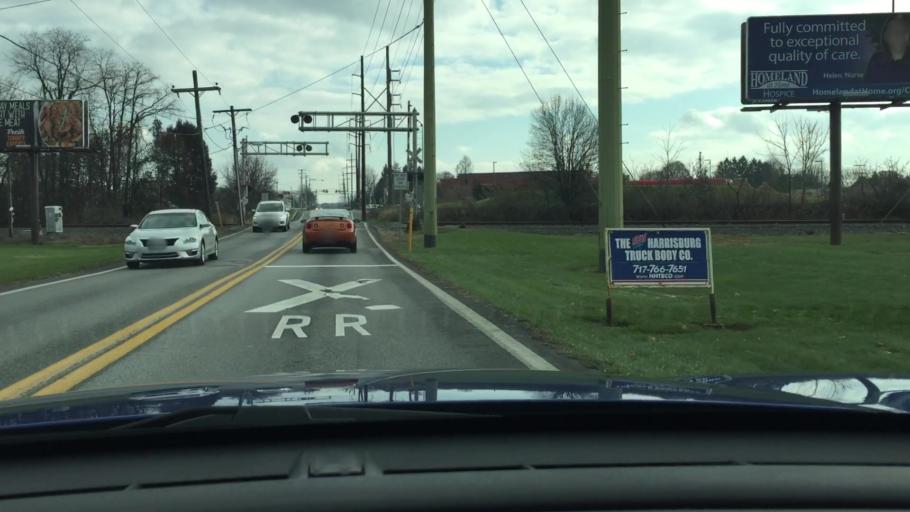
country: US
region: Pennsylvania
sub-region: Cumberland County
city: Shiremanstown
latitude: 40.2201
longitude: -76.9804
